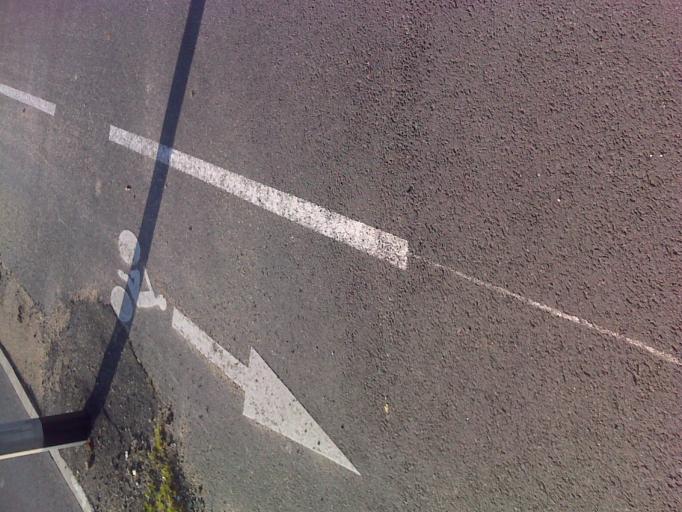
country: FR
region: Poitou-Charentes
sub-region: Departement de la Charente-Maritime
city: Rochefort
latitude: 45.9513
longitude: -0.9555
